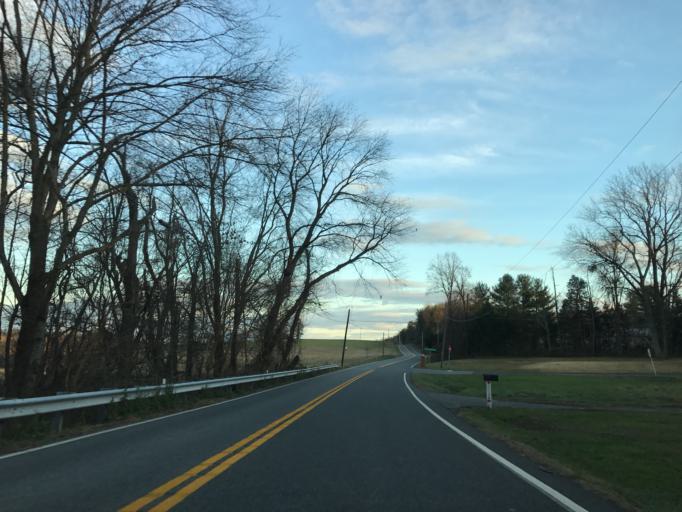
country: US
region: Pennsylvania
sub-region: York County
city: Susquehanna Trails
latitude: 39.7070
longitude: -76.2587
